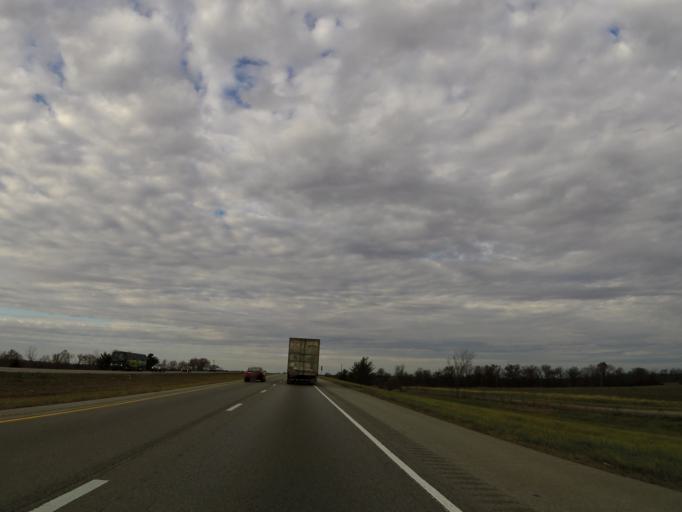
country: US
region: Illinois
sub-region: Clinton County
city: Wamac
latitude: 38.3621
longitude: -89.0666
